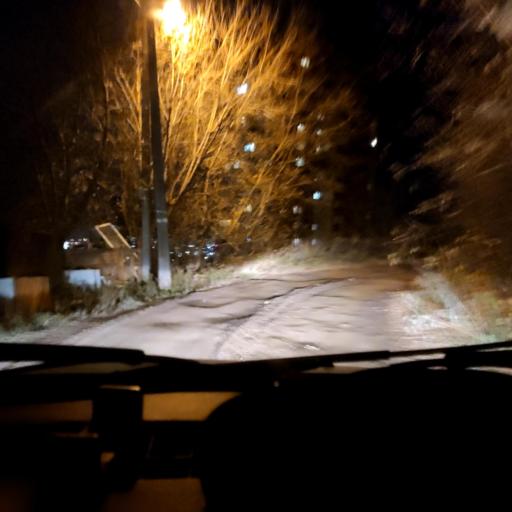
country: RU
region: Bashkortostan
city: Ufa
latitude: 54.7788
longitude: 56.0460
